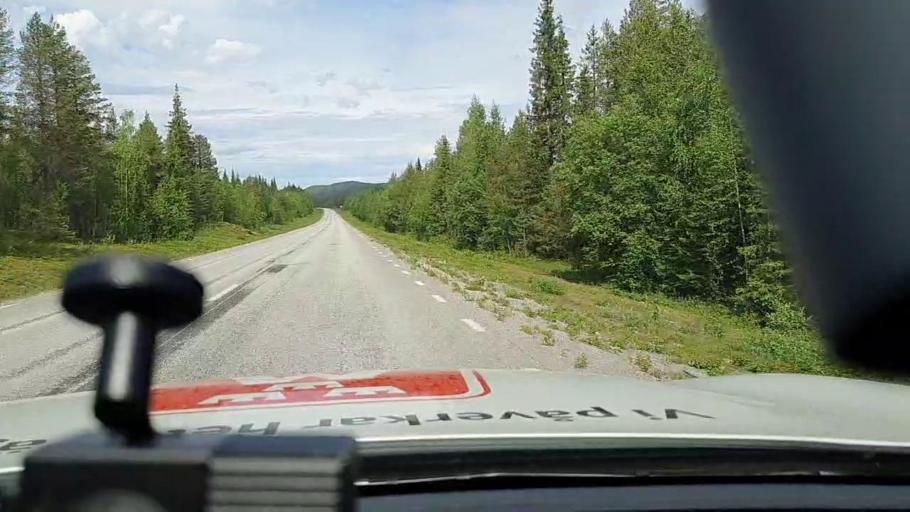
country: SE
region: Norrbotten
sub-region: Jokkmokks Kommun
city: Jokkmokk
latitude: 66.5479
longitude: 20.1283
